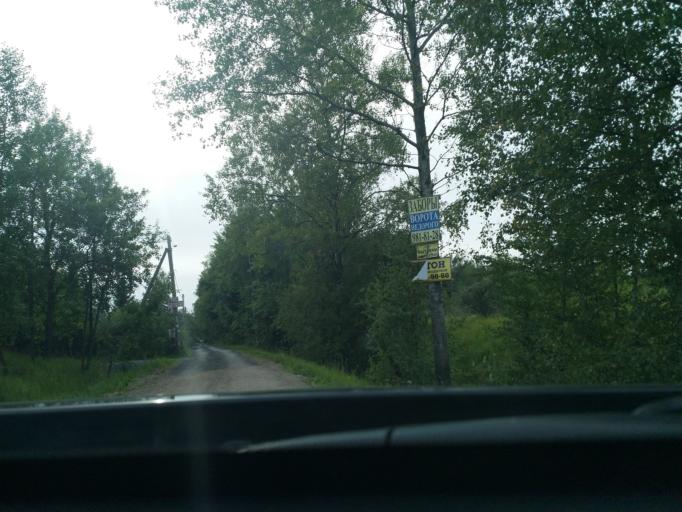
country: RU
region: Leningrad
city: Nikol'skoye
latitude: 59.7269
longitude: 30.7771
